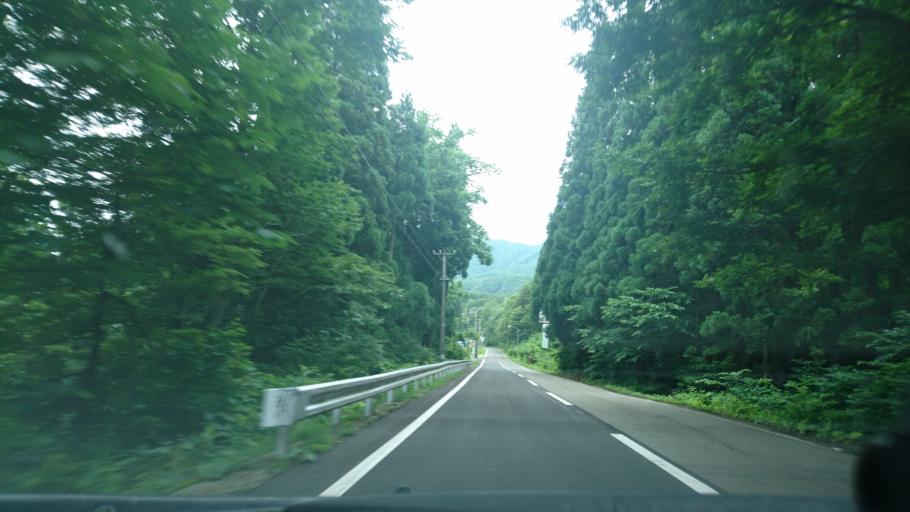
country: JP
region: Akita
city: Yuzawa
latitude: 39.1714
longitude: 140.7347
